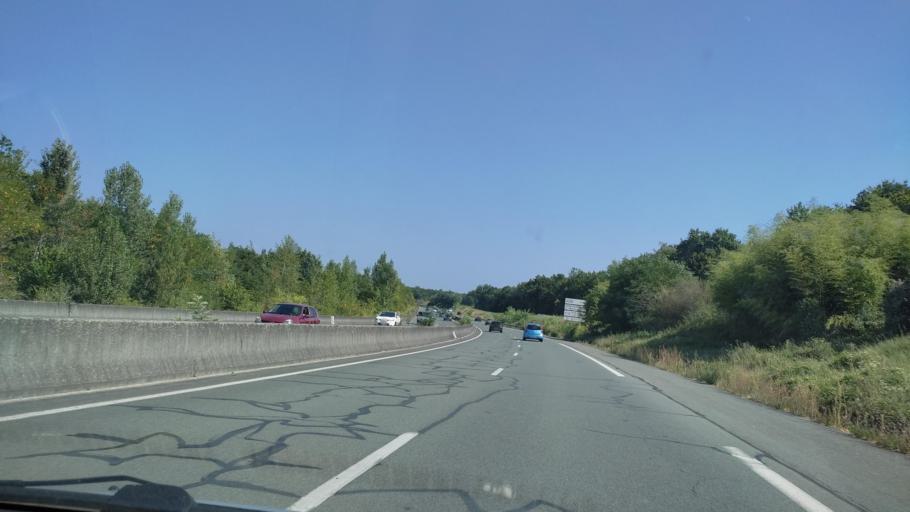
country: FR
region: Poitou-Charentes
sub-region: Departement de la Charente
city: Saint-Yrieix-sur-Charente
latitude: 45.6835
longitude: 0.1169
